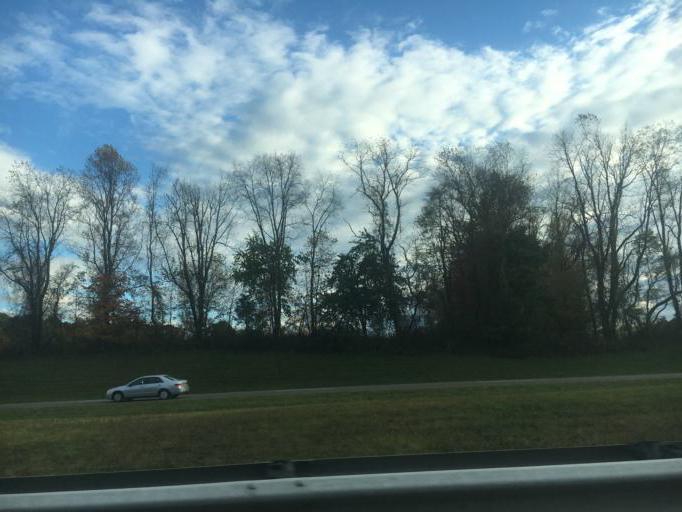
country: US
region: Virginia
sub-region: Washington County
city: Emory
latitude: 36.7680
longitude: -81.8255
